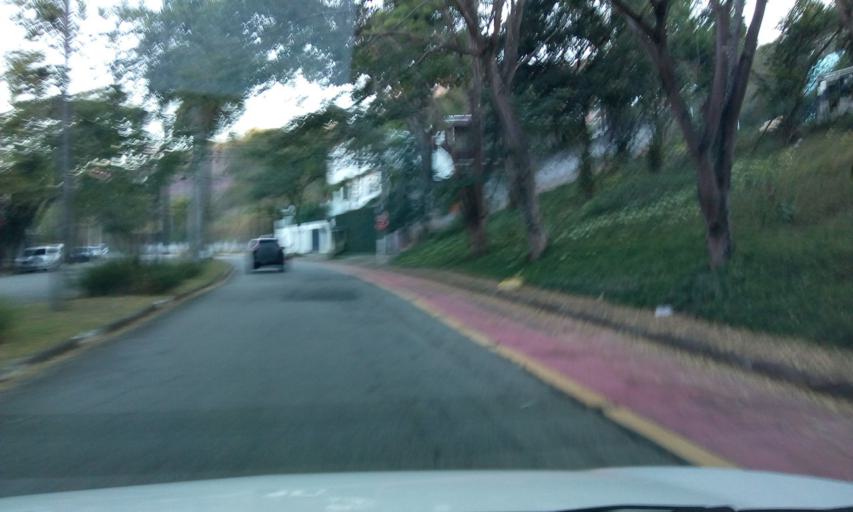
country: BR
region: Sao Paulo
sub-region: Sao Paulo
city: Sao Paulo
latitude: -23.5901
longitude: -46.7018
